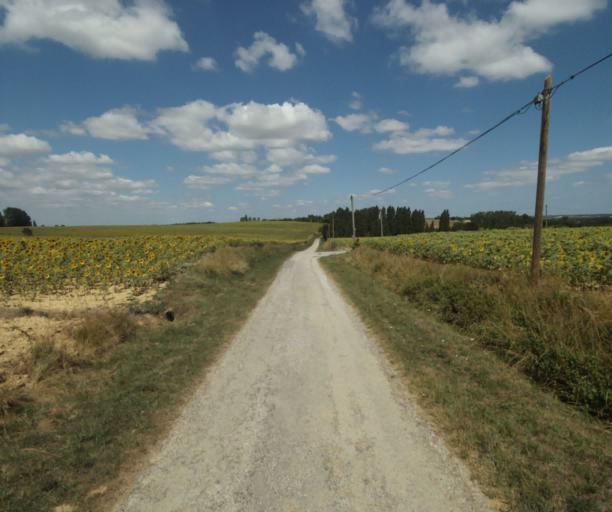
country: FR
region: Midi-Pyrenees
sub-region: Departement de la Haute-Garonne
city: Saint-Felix-Lauragais
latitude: 43.4659
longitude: 1.8414
